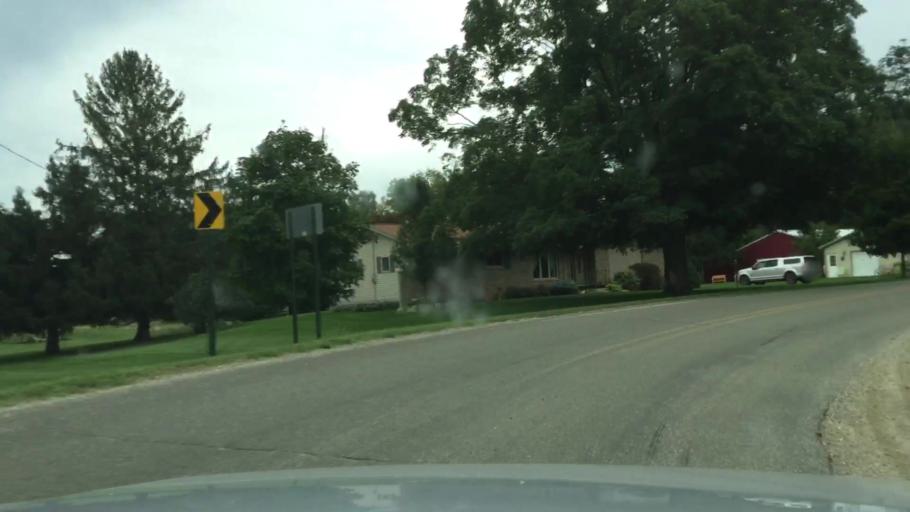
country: US
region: Michigan
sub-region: Shiawassee County
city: Durand
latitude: 42.8298
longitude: -84.0129
